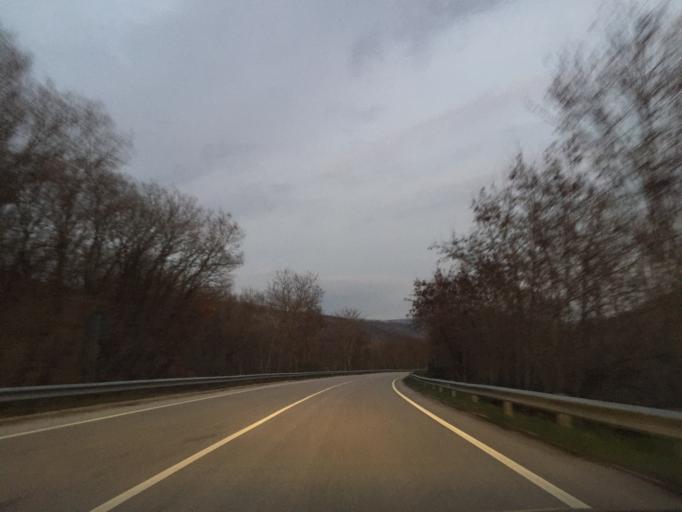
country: IT
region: Apulia
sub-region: Provincia di Foggia
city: San Marco la Catola
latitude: 41.5044
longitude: 15.0131
